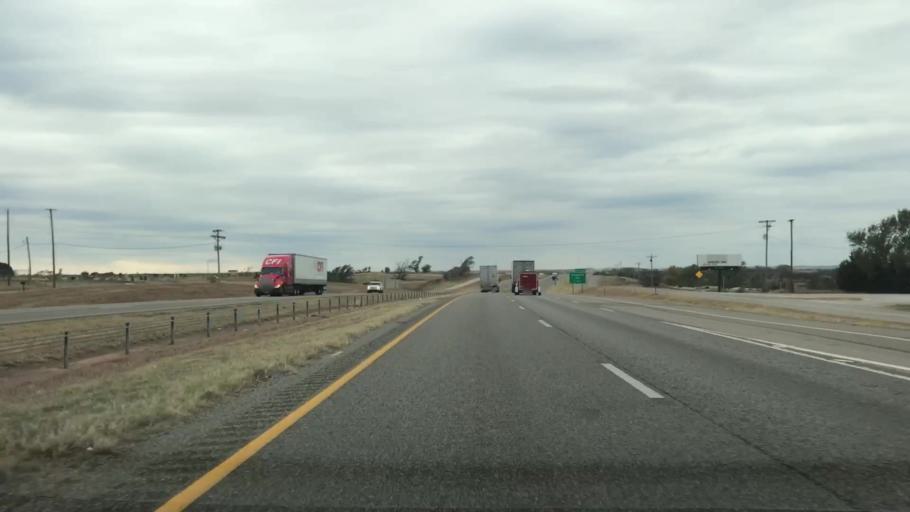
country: US
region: Oklahoma
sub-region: Custer County
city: Clinton
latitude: 35.4803
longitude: -99.0277
